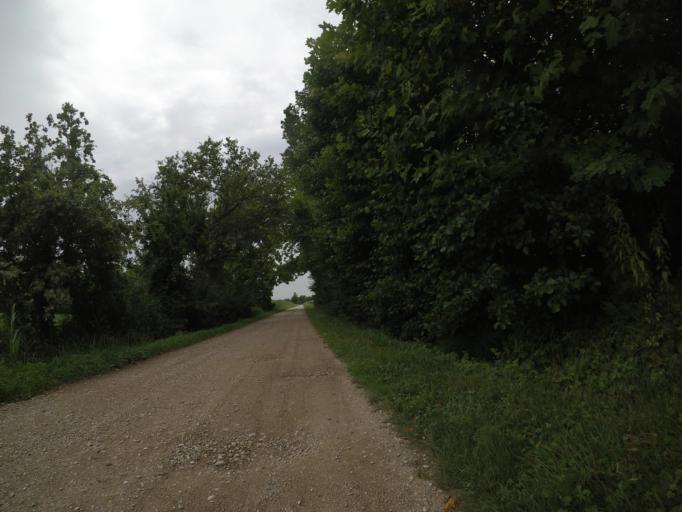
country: IT
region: Friuli Venezia Giulia
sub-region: Provincia di Udine
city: Bertiolo
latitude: 45.9082
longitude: 13.0614
